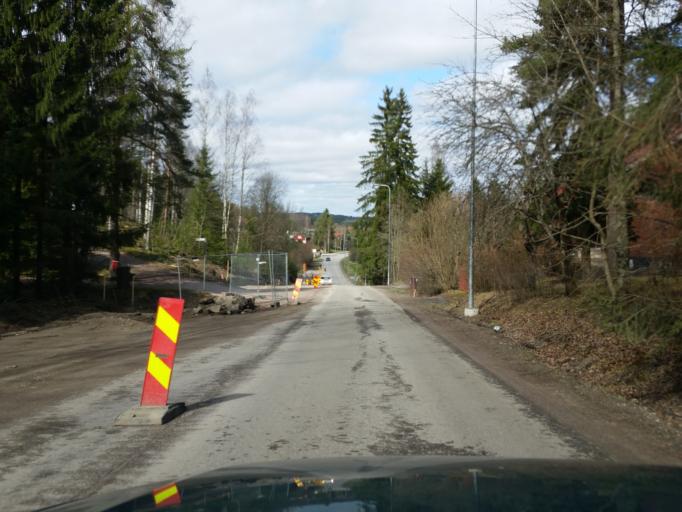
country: FI
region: Uusimaa
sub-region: Helsinki
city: Vihti
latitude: 60.4073
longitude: 24.3312
